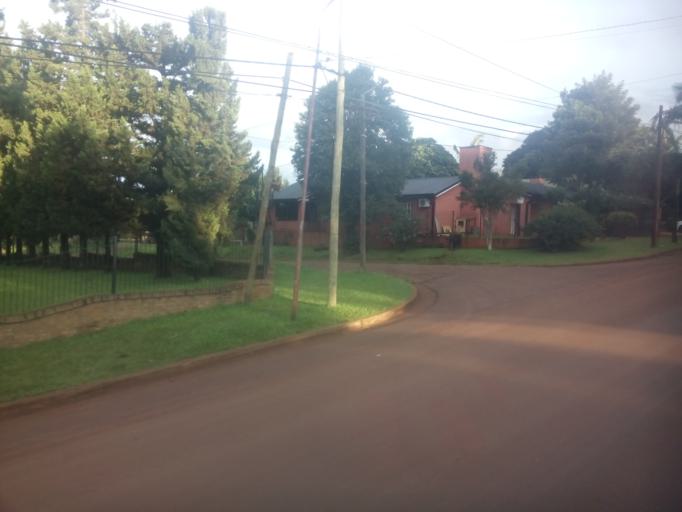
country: AR
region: Misiones
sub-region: Departamento de Obera
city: Obera
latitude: -27.4900
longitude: -55.1462
